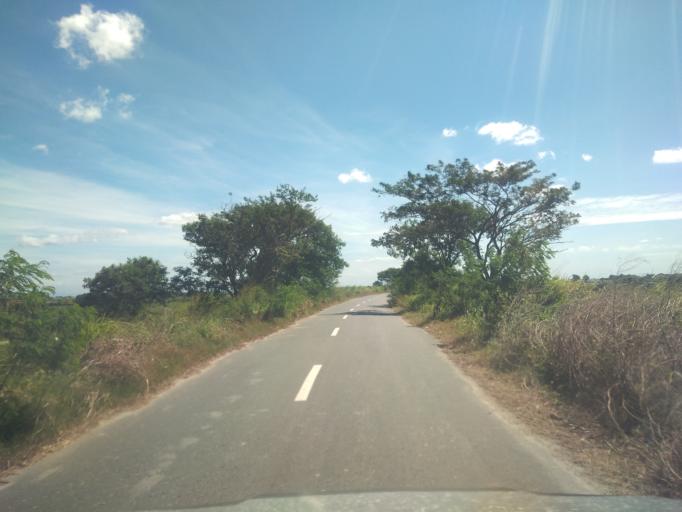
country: PH
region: Central Luzon
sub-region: Province of Pampanga
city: Balas
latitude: 15.0487
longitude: 120.5893
